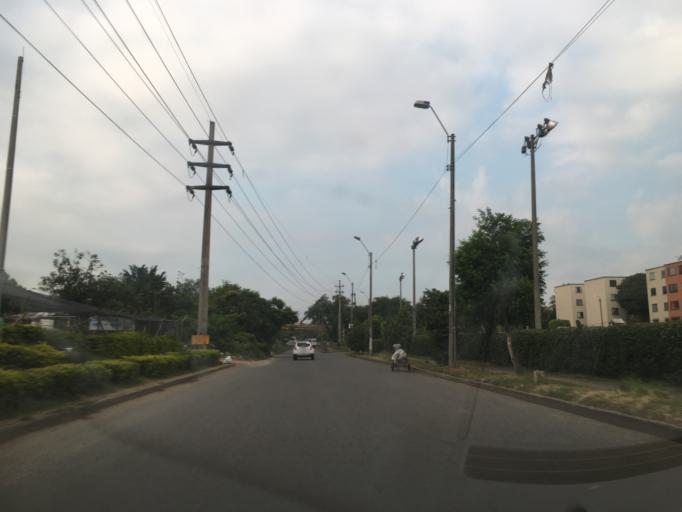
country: CO
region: Valle del Cauca
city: Cali
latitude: 3.4032
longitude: -76.5232
